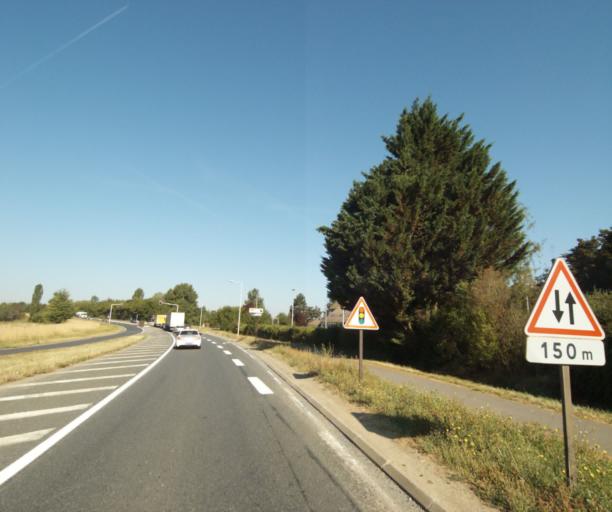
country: FR
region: Ile-de-France
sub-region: Departement de Seine-et-Marne
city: Moissy-Cramayel
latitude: 48.6259
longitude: 2.5758
